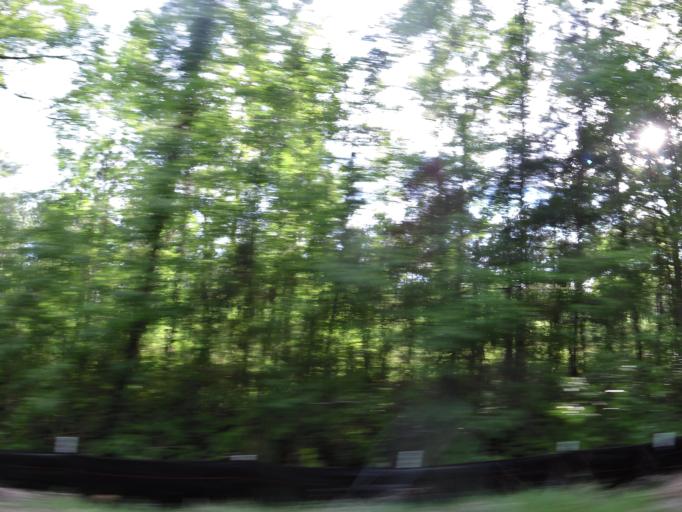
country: US
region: South Carolina
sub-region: Jasper County
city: Ridgeland
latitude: 32.5079
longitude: -81.1404
